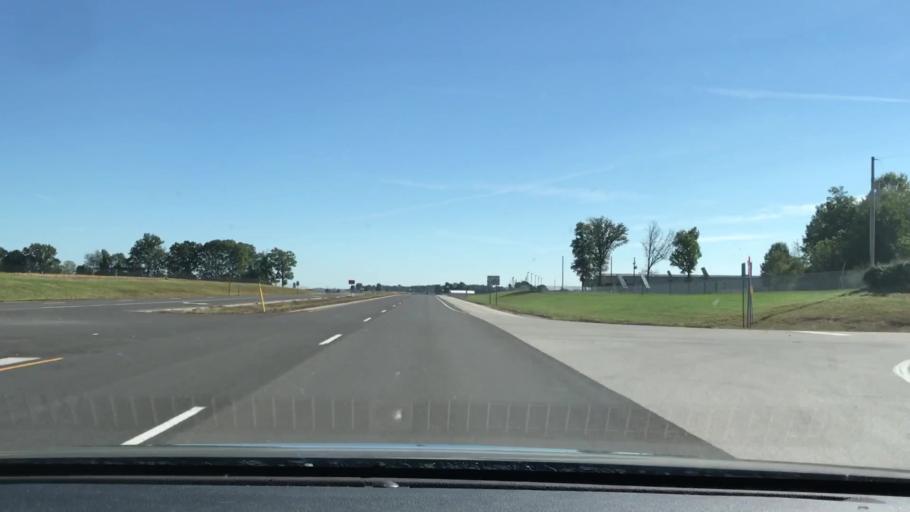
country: US
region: Kentucky
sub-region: Todd County
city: Elkton
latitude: 36.8045
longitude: -87.0675
